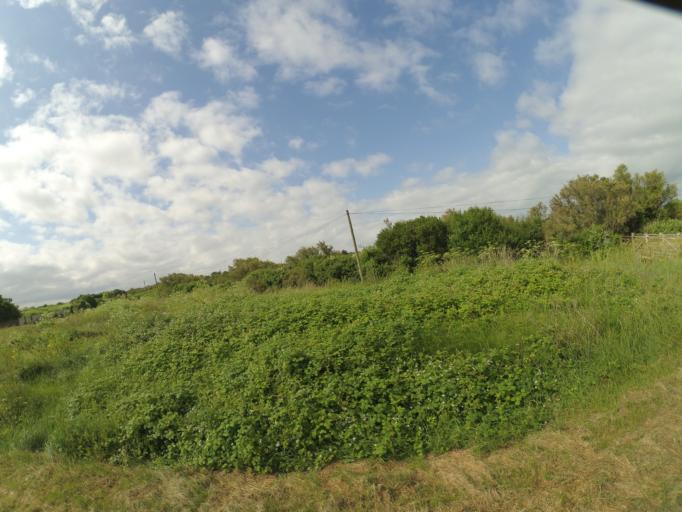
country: FR
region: Poitou-Charentes
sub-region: Departement de la Charente-Maritime
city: Angoulins
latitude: 46.1095
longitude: -1.1178
